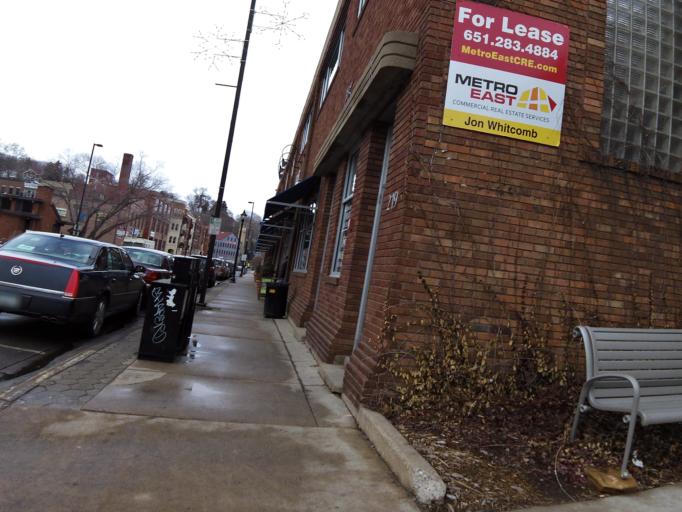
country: US
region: Minnesota
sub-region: Washington County
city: Stillwater
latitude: 45.0575
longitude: -92.8064
